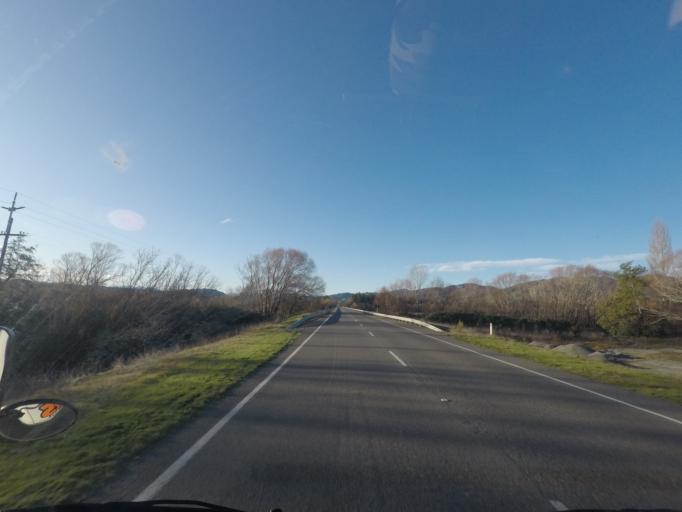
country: NZ
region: Canterbury
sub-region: Kaikoura District
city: Kaikoura
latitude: -42.7245
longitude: 173.2815
